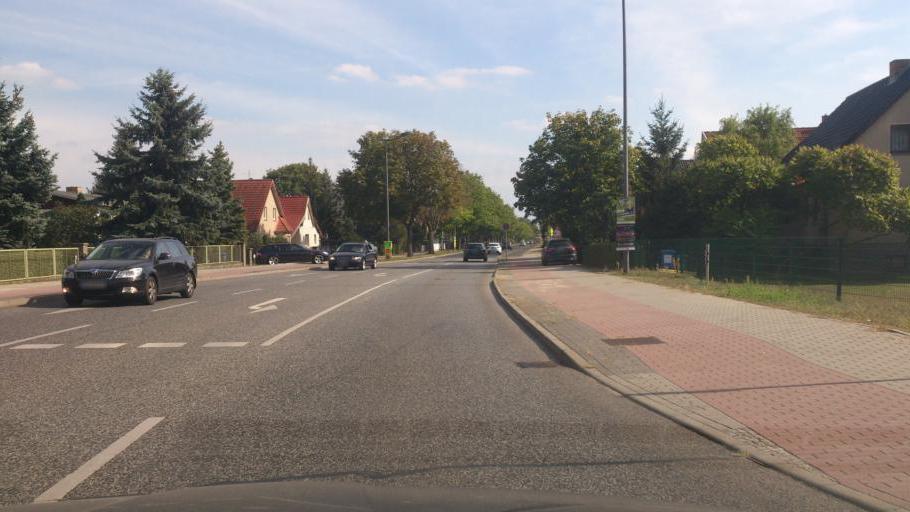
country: DE
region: Brandenburg
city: Ludwigsfelde
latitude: 52.3160
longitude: 13.2359
